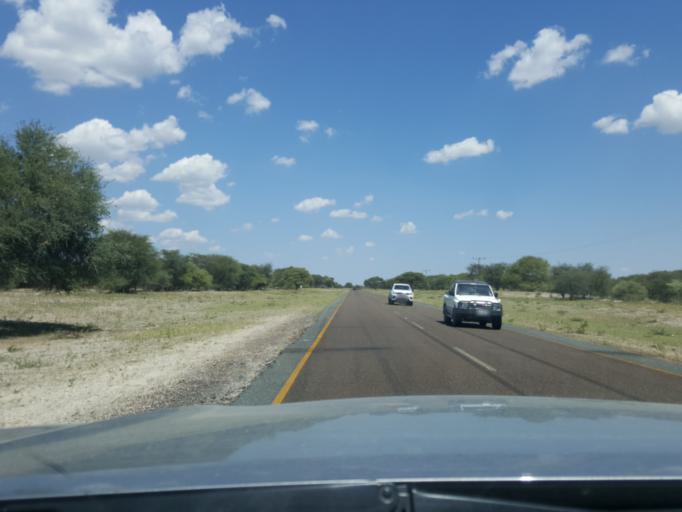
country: BW
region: North West
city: Maun
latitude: -20.1554
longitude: 23.2707
